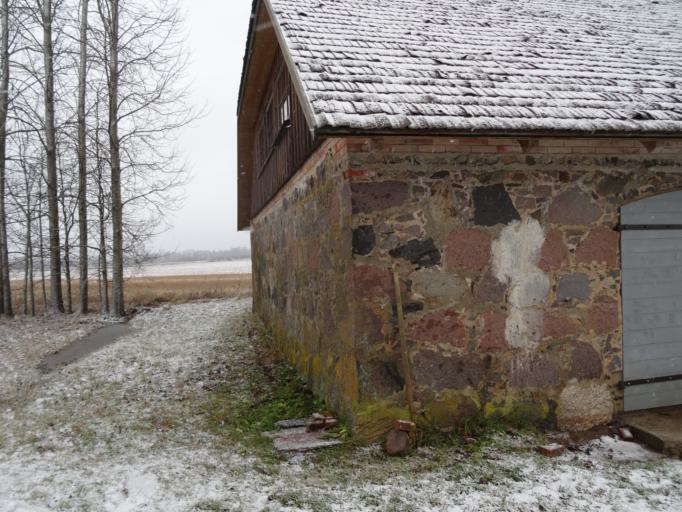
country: LV
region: Broceni
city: Broceni
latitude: 56.8431
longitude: 22.3824
